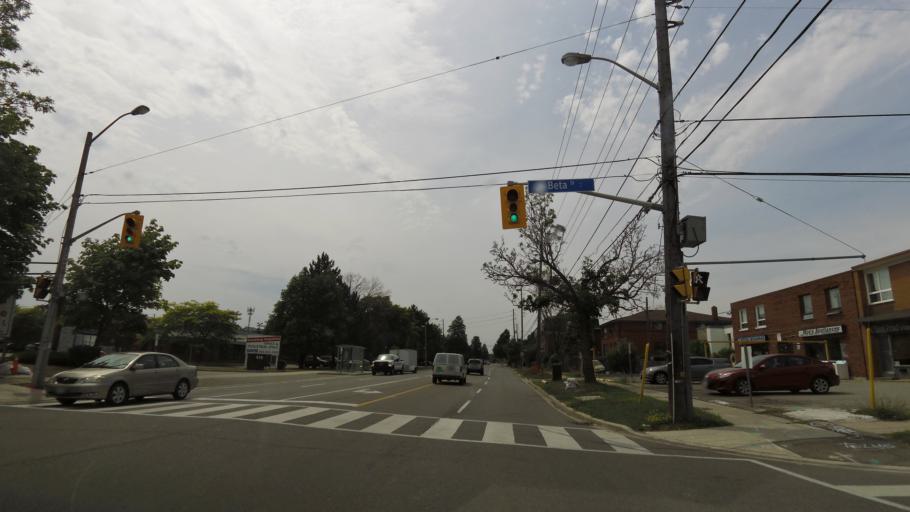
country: CA
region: Ontario
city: Etobicoke
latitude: 43.6033
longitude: -79.5384
